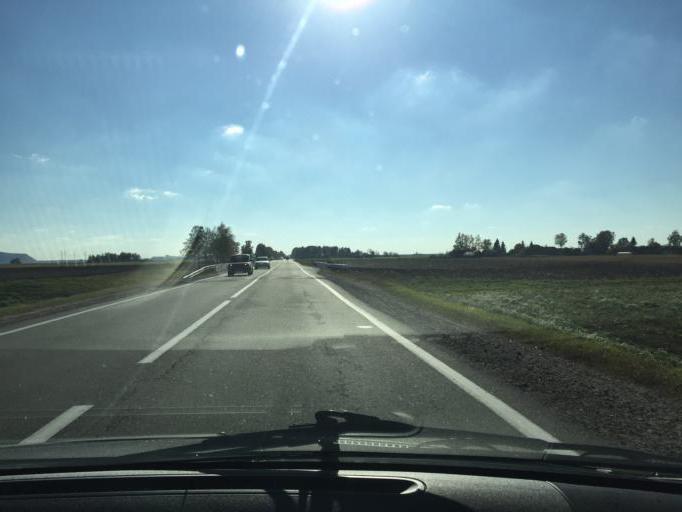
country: BY
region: Minsk
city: Slutsk
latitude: 52.9179
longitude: 27.4822
